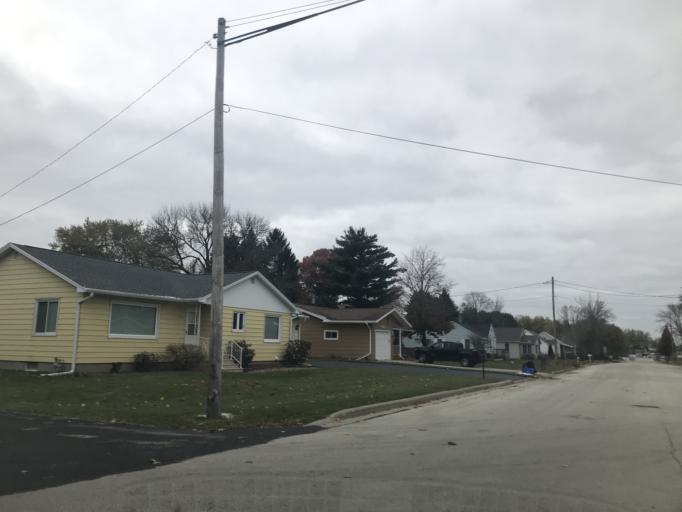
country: US
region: Wisconsin
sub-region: Marinette County
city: Marinette
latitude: 45.0963
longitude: -87.6510
